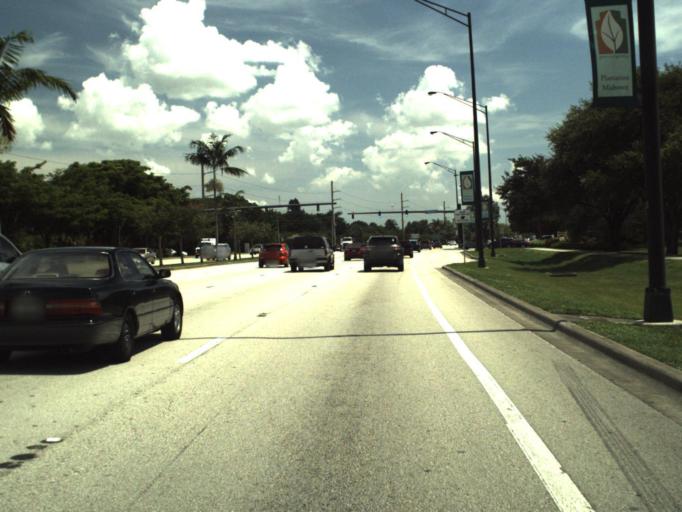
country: US
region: Florida
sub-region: Broward County
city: Plantation
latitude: 26.1163
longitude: -80.2512
